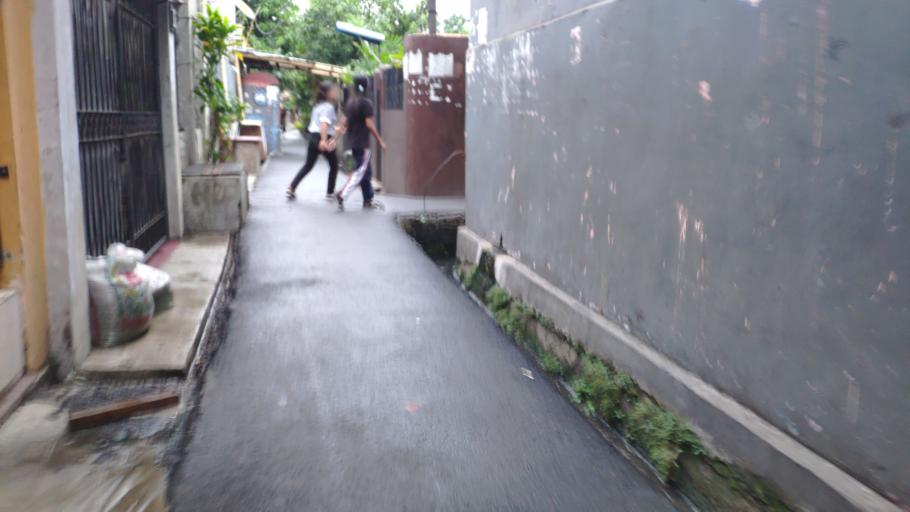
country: ID
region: Jakarta Raya
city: Jakarta
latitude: -6.2058
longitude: 106.8681
